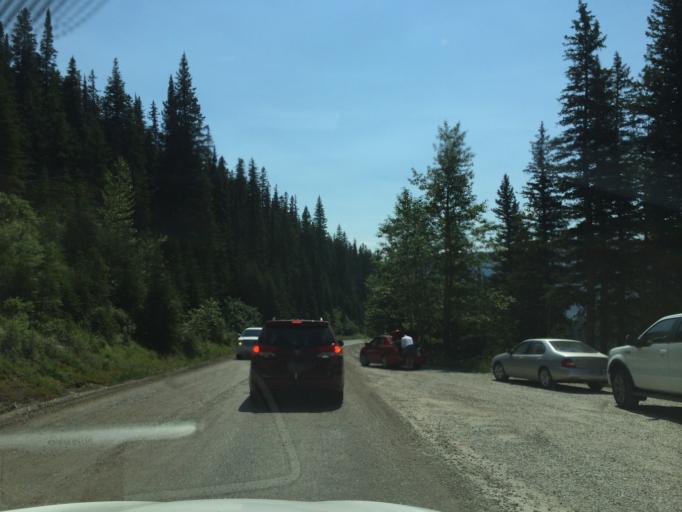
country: US
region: Montana
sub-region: Flathead County
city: Columbia Falls
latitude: 48.6982
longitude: -113.6673
